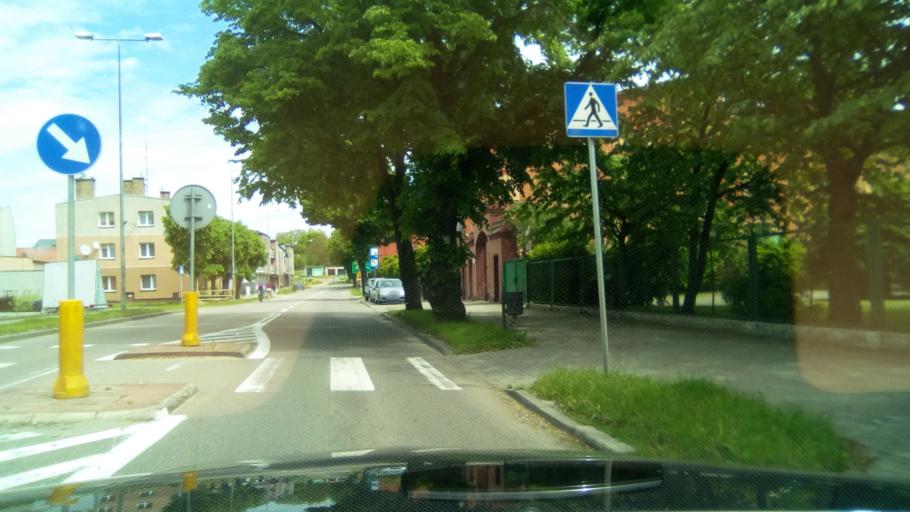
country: PL
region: Pomeranian Voivodeship
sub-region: Powiat leborski
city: Lebork
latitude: 54.5452
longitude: 17.7487
